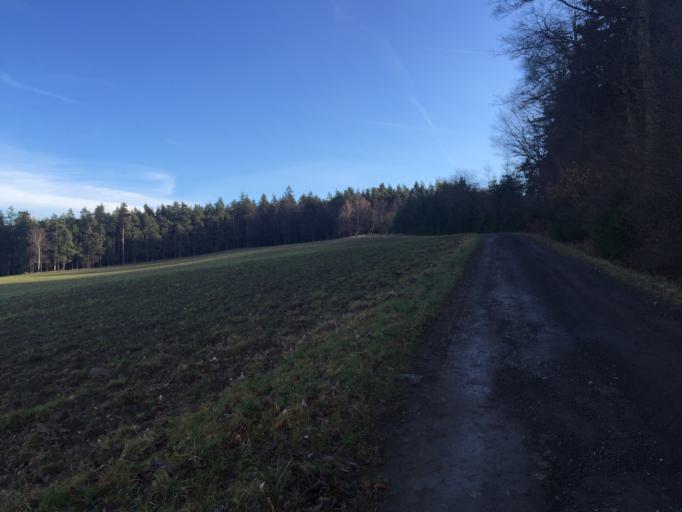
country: DE
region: Thuringia
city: Doschnitz
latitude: 50.6505
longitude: 11.2479
